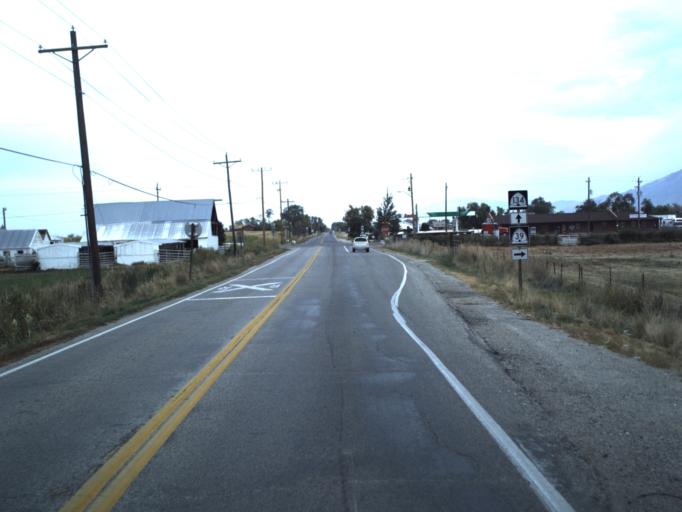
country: US
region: Utah
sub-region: Weber County
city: Plain City
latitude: 41.2444
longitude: -112.0926
